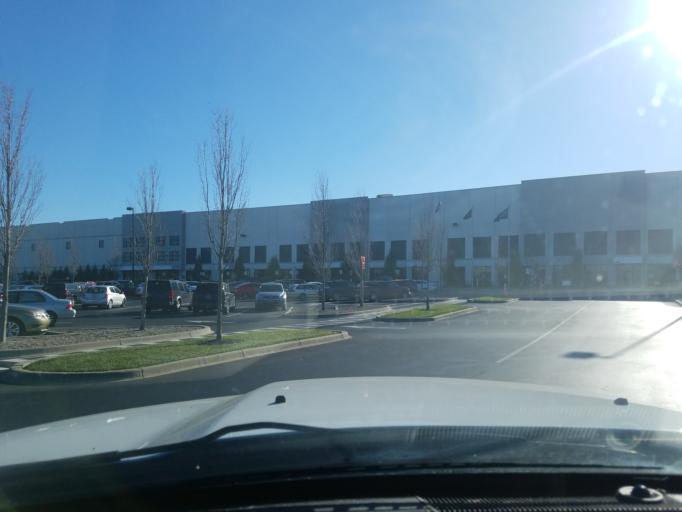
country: US
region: Indiana
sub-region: Clark County
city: Sellersburg
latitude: 38.3802
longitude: -85.6861
